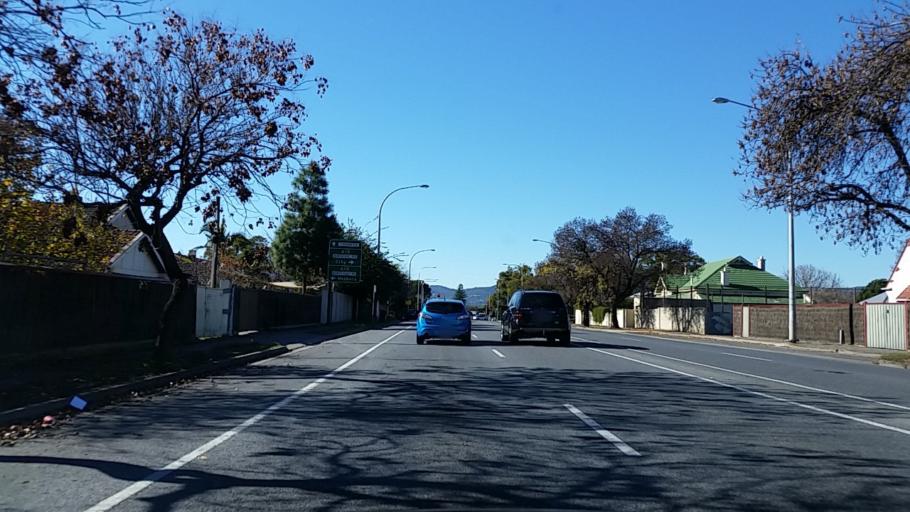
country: AU
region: South Australia
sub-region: Prospect
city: Prospect
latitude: -34.8934
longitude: 138.6068
